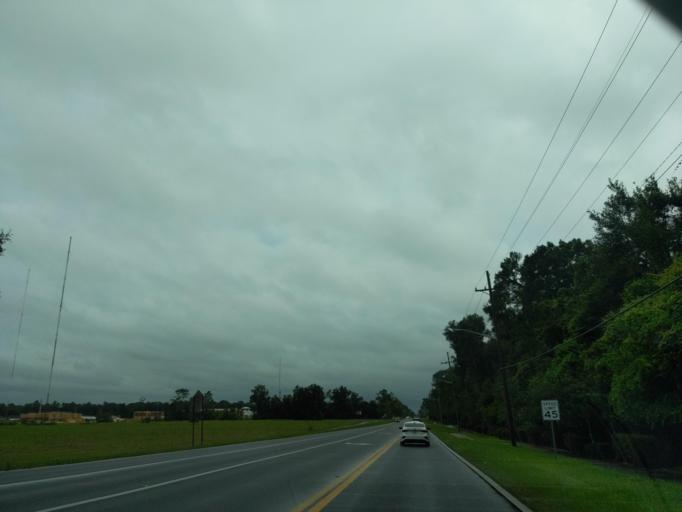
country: US
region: Florida
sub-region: Alachua County
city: Gainesville
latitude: 29.6445
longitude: -82.4225
